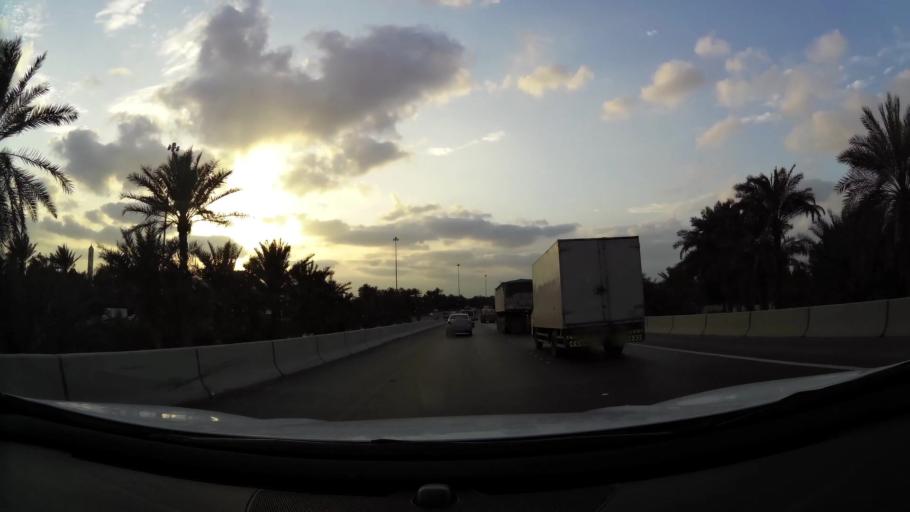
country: AE
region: Abu Dhabi
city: Abu Dhabi
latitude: 24.4075
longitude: 54.5211
